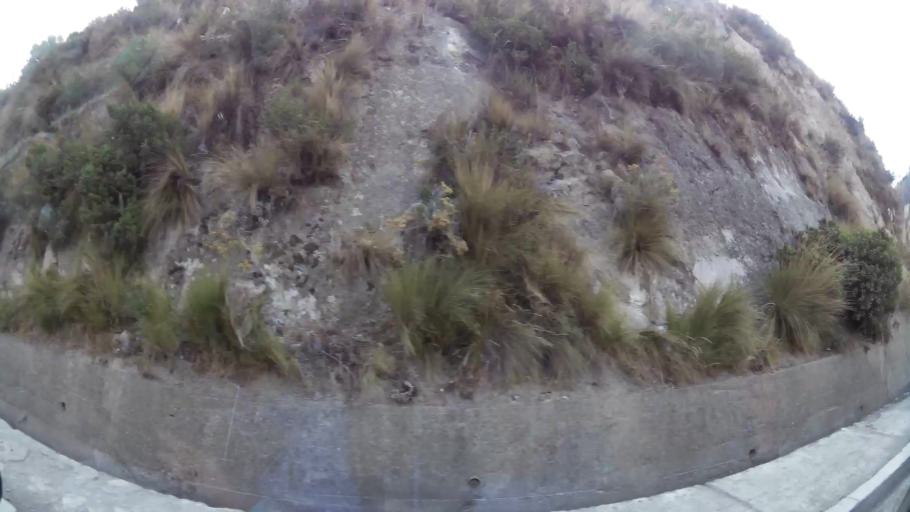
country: BO
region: La Paz
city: La Paz
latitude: -16.4680
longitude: -68.1194
